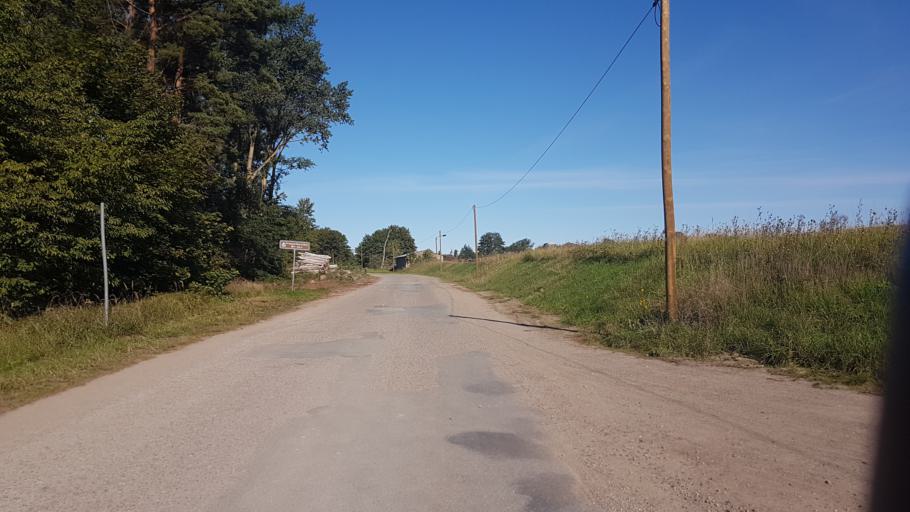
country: DE
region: Mecklenburg-Vorpommern
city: Sagard
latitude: 54.5236
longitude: 13.5175
